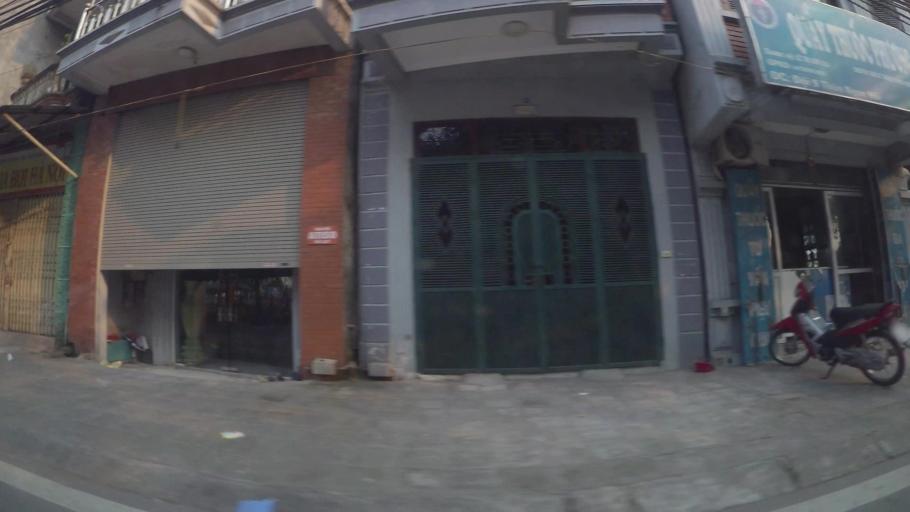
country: VN
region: Ha Noi
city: Van Dien
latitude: 20.9242
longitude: 105.8499
